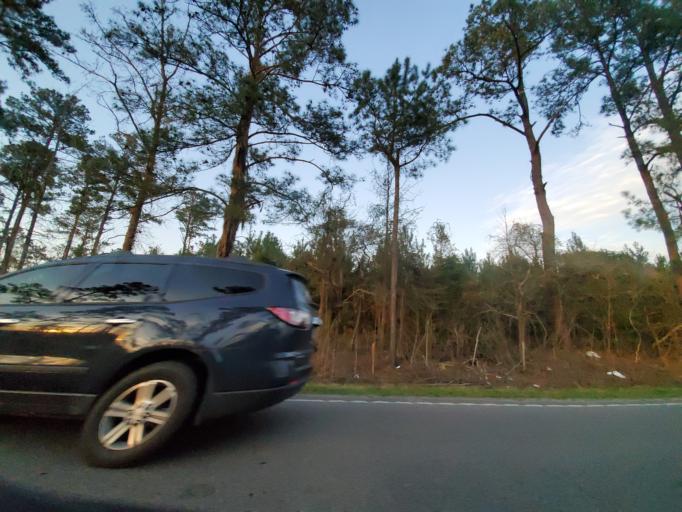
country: US
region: South Carolina
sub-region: Dorchester County
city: Ridgeville
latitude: 32.9962
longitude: -80.3142
